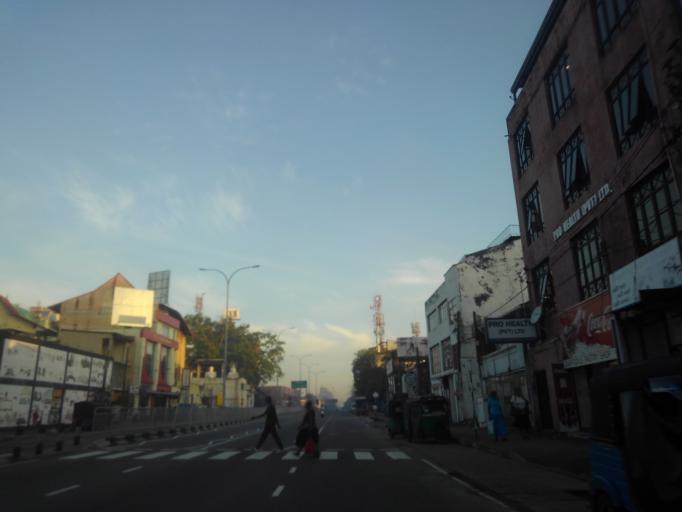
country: LK
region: Western
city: Pita Kotte
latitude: 6.8951
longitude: 79.8771
